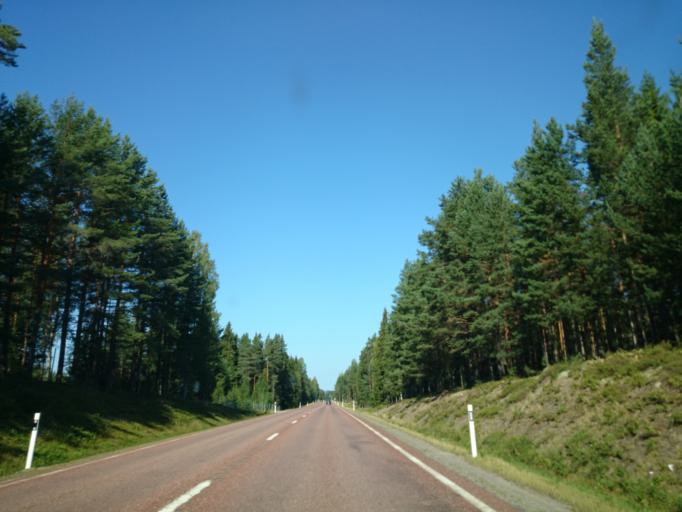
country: SE
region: Gaevleborg
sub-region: Hudiksvalls Kommun
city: Delsbo
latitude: 61.7926
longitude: 16.5852
